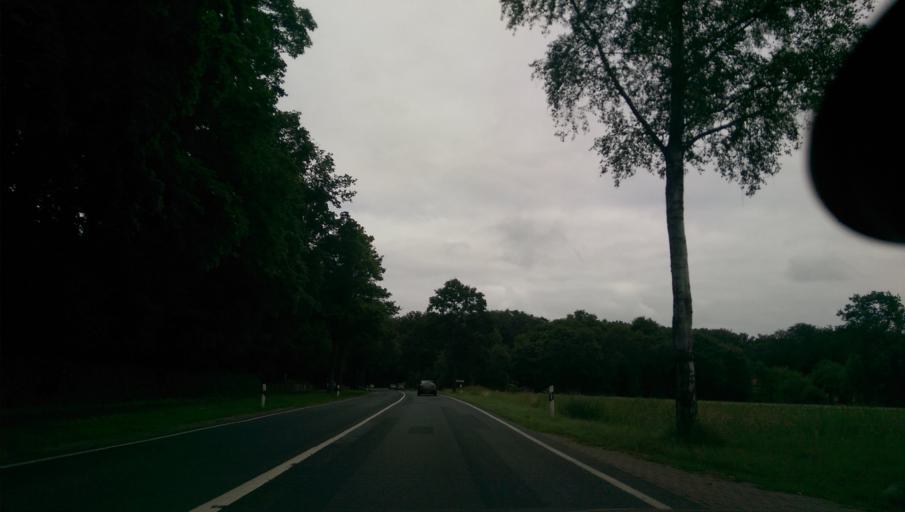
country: DE
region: Lower Saxony
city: Botersen
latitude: 53.1349
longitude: 9.3627
